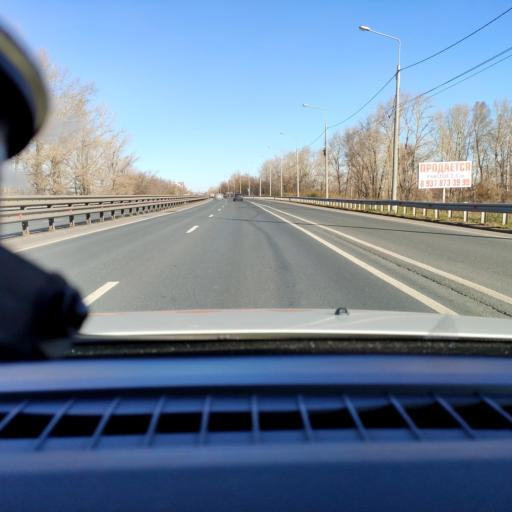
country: RU
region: Samara
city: Samara
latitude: 53.1018
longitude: 50.1617
